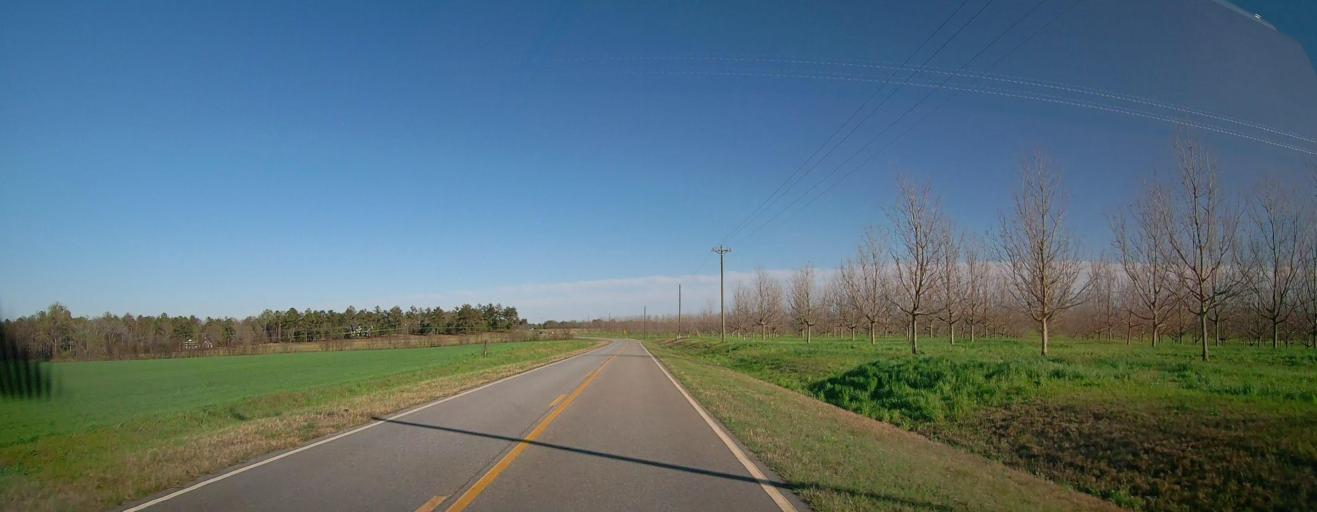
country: US
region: Georgia
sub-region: Dooly County
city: Unadilla
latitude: 32.3533
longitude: -83.6312
